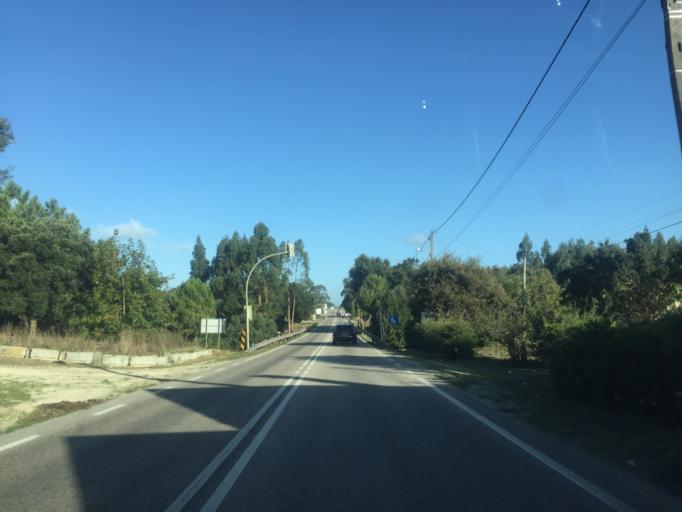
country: PT
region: Leiria
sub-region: Alcobaca
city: Benedita
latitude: 39.3992
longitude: -8.9605
